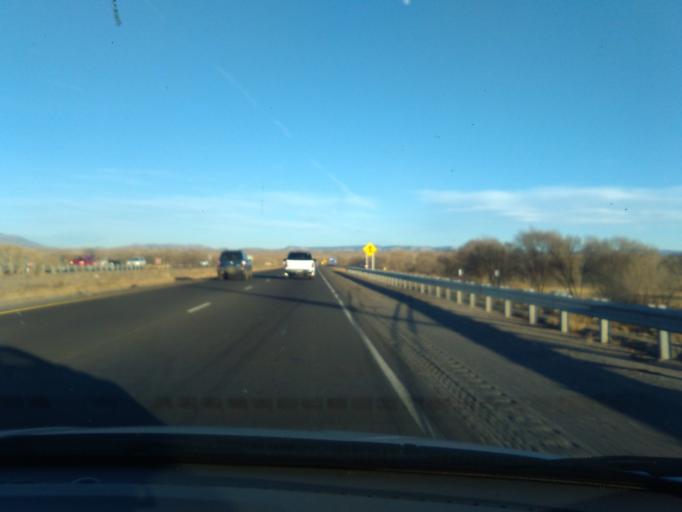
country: US
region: New Mexico
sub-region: Bernalillo County
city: South Valley
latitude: 34.9483
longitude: -106.6931
